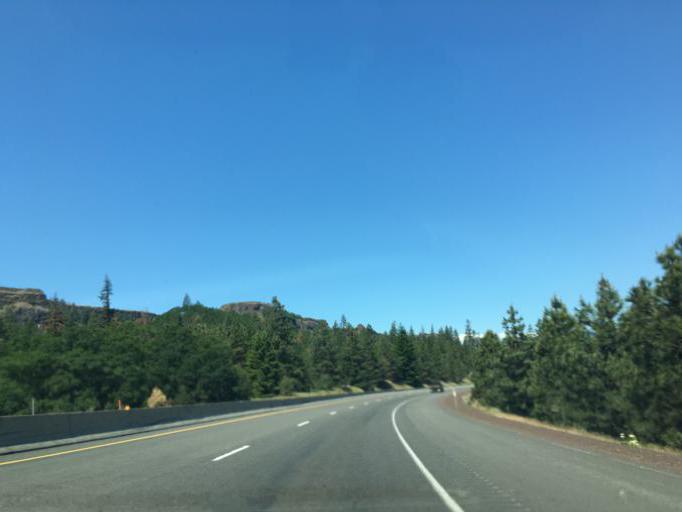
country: US
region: Oregon
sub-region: Wasco County
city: Chenoweth
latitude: 45.6776
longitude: -121.2874
